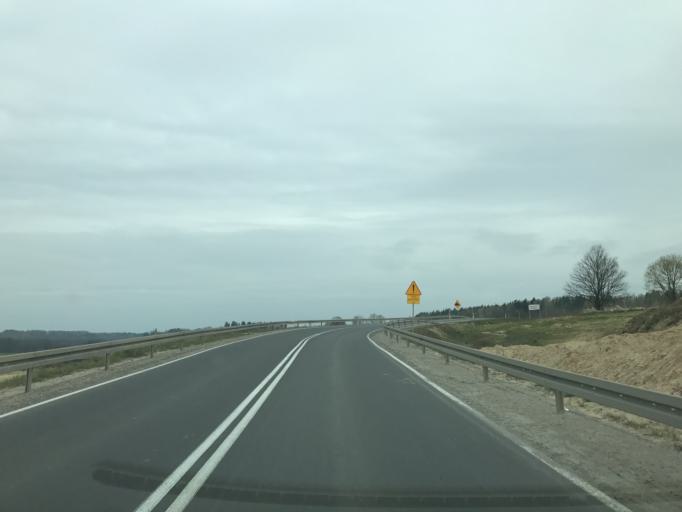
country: PL
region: Warmian-Masurian Voivodeship
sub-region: Powiat ostrodzki
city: Gierzwald
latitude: 53.5980
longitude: 20.0806
